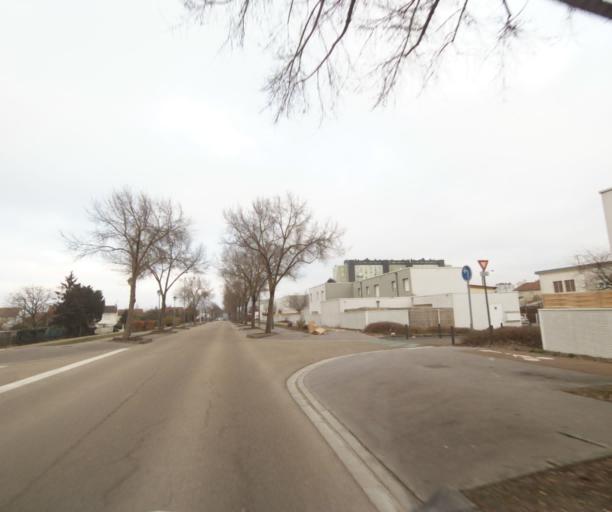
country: FR
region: Champagne-Ardenne
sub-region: Departement de la Haute-Marne
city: Bettancourt-la-Ferree
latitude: 48.6379
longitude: 4.9740
